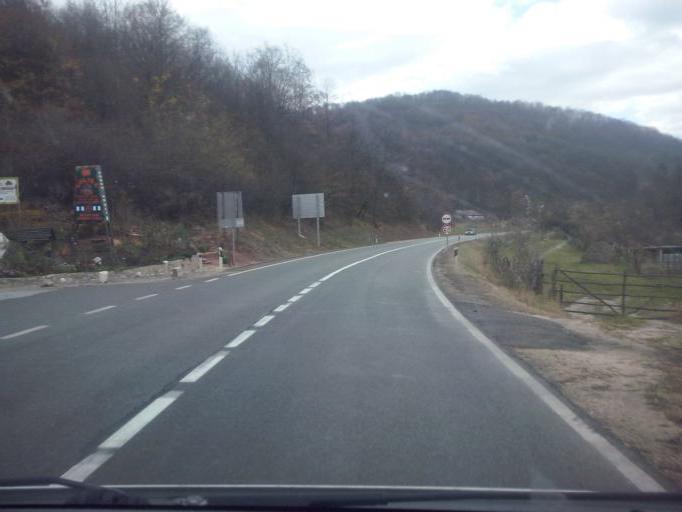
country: RS
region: Central Serbia
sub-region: Nisavski Okrug
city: Razanj
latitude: 43.8597
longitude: 21.6237
